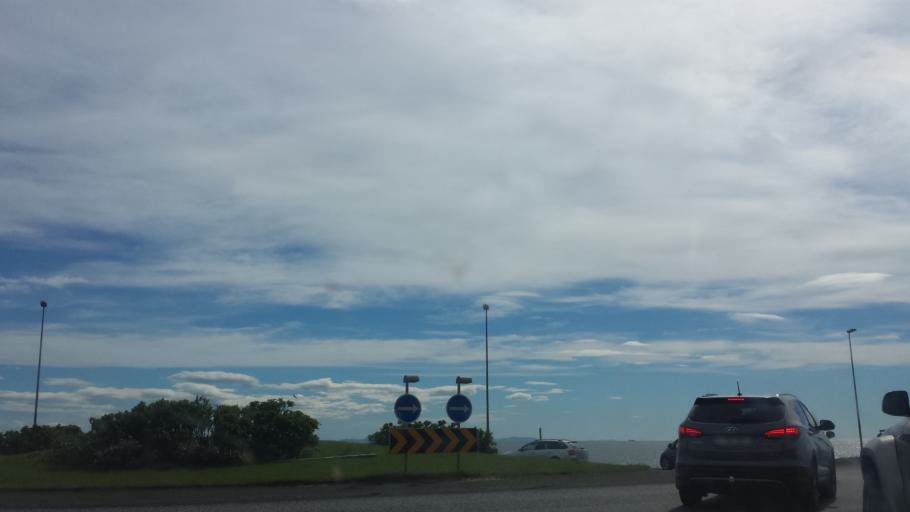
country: IS
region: West
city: Akranes
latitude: 64.3085
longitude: -21.9122
